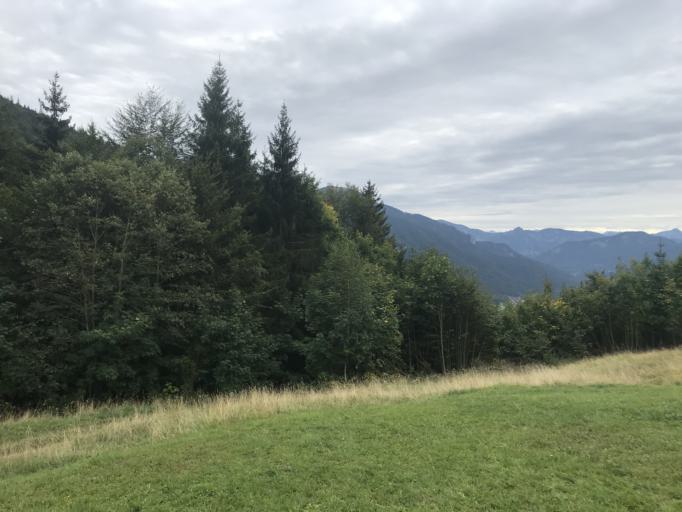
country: DE
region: Bavaria
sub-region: Upper Bavaria
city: Rottach-Egern
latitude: 47.7035
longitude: 11.7882
